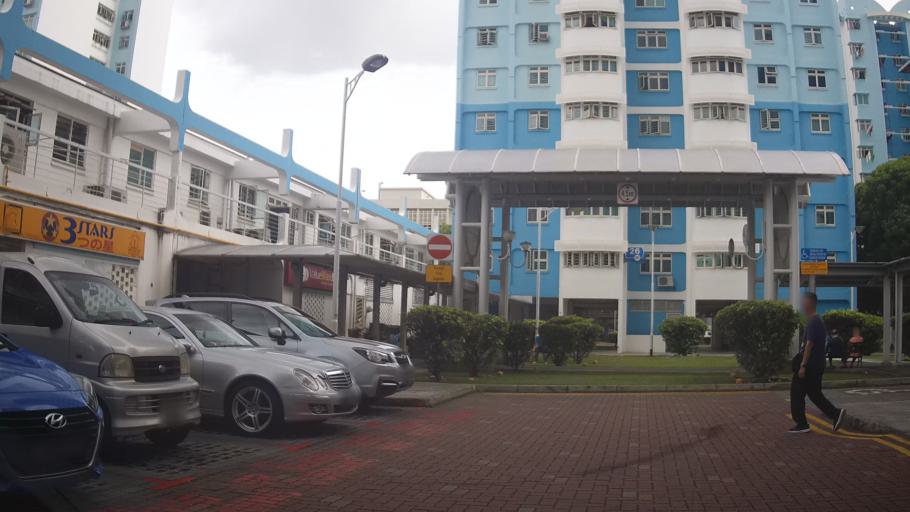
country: SG
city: Singapore
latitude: 1.3186
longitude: 103.8627
